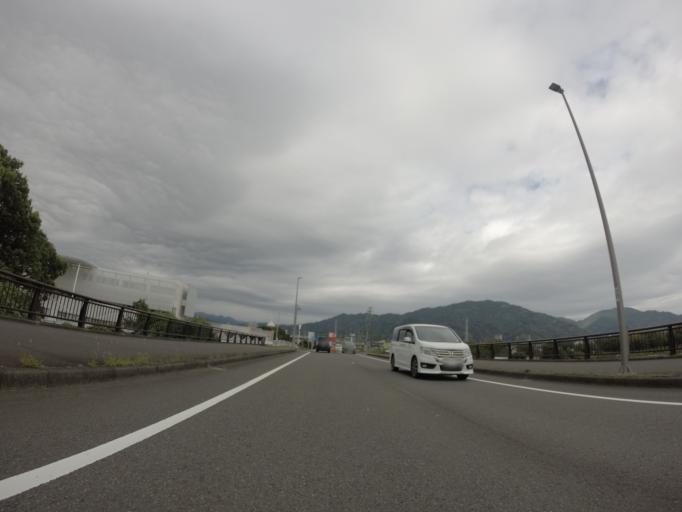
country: JP
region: Shizuoka
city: Yaizu
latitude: 34.8756
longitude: 138.3059
